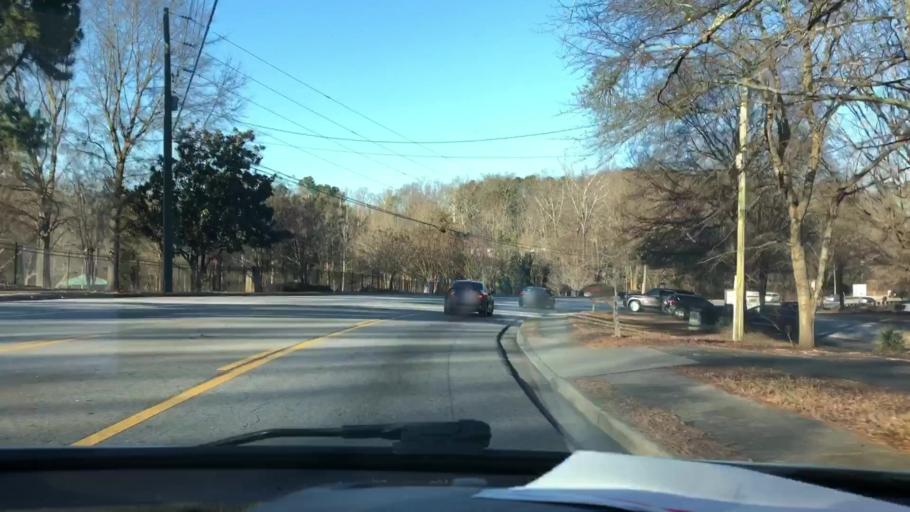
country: US
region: Georgia
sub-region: Gwinnett County
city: Snellville
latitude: 33.8948
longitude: -84.0555
